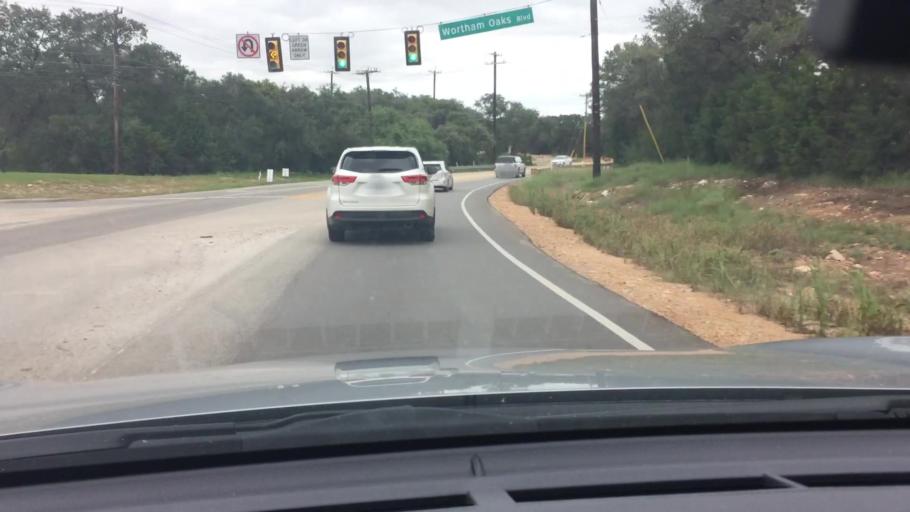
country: US
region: Texas
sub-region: Comal County
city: Garden Ridge
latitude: 29.6406
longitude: -98.3786
